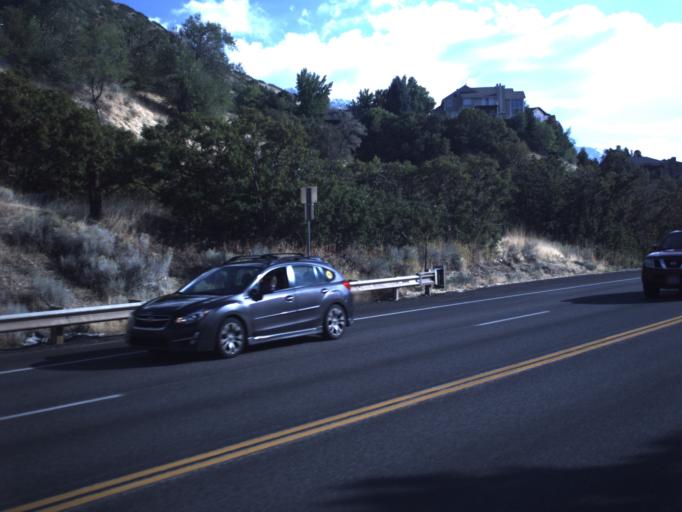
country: US
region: Utah
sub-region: Salt Lake County
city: Cottonwood Heights
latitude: 40.6122
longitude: -111.7903
